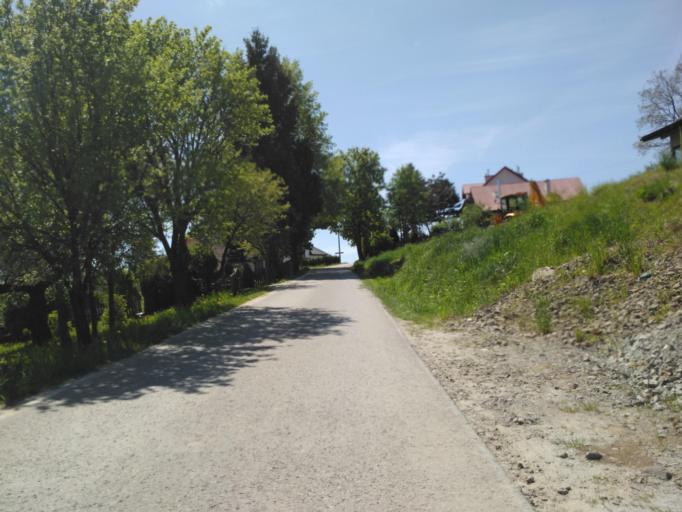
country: PL
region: Subcarpathian Voivodeship
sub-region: Powiat krosnienski
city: Iwonicz-Zdroj
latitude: 49.5456
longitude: 21.7779
